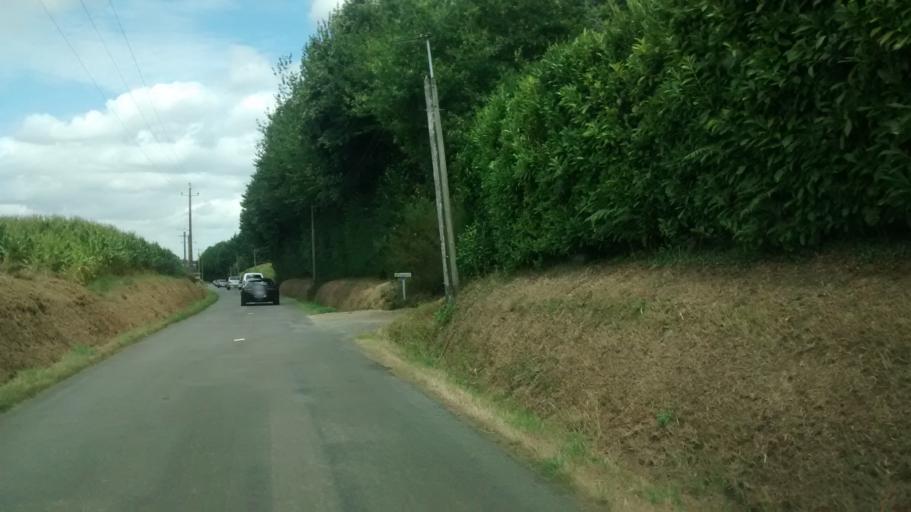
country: FR
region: Brittany
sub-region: Departement d'Ille-et-Vilaine
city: Tinteniac
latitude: 48.3008
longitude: -1.8471
